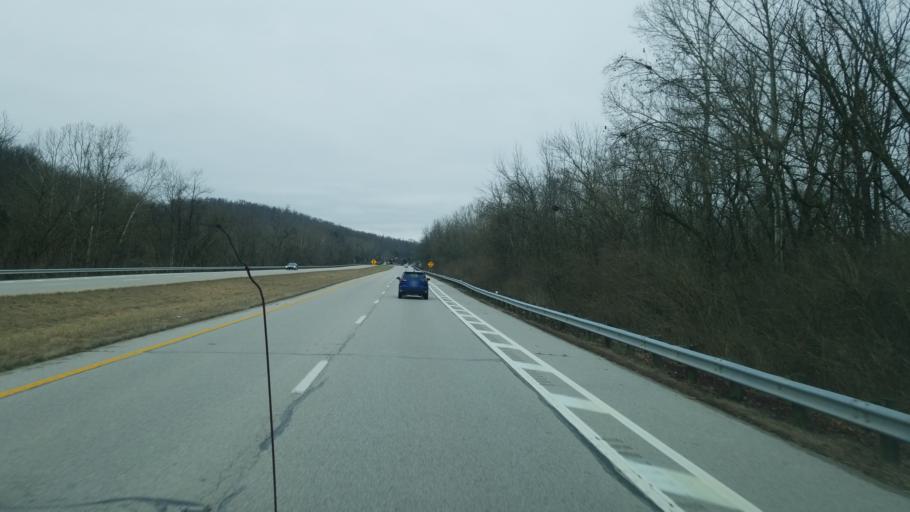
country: US
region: Ohio
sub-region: Clermont County
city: Withamsville
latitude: 39.0139
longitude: -84.3073
